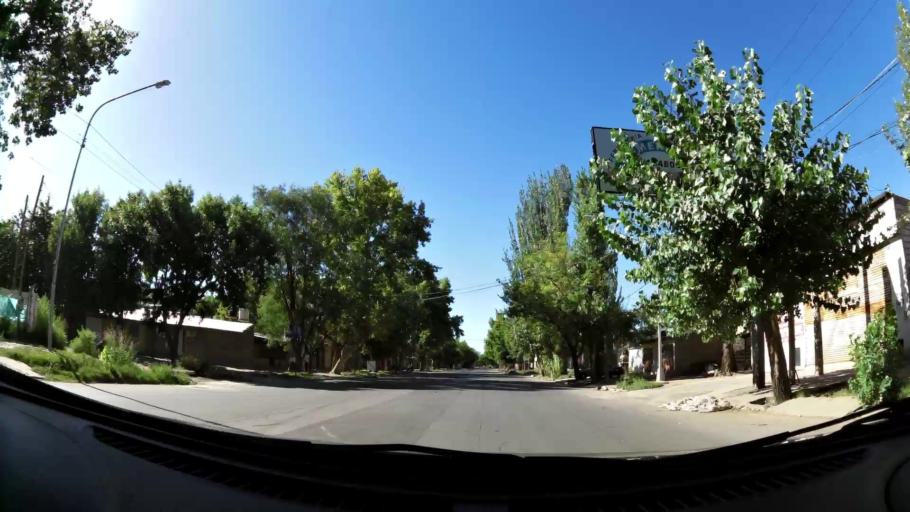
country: AR
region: Mendoza
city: Las Heras
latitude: -32.8469
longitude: -68.8204
